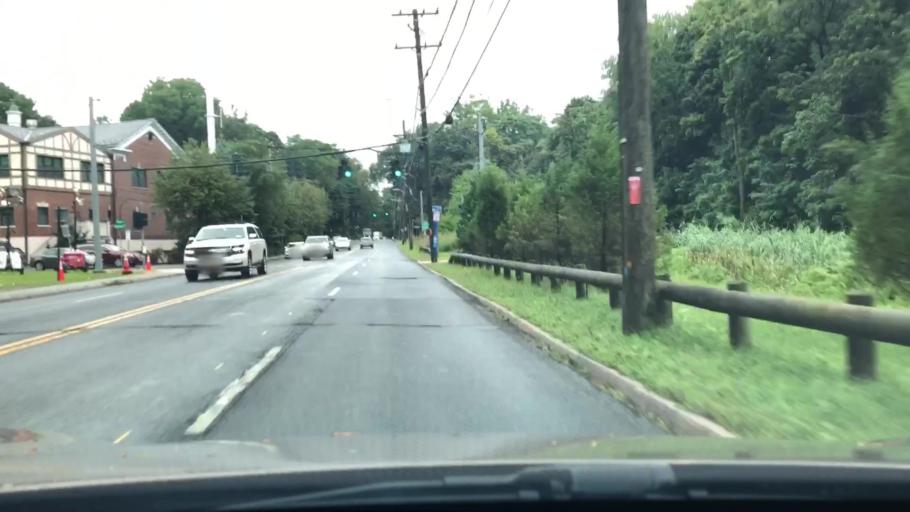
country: US
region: New York
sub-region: Westchester County
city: Scarsdale
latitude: 41.0043
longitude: -73.7848
